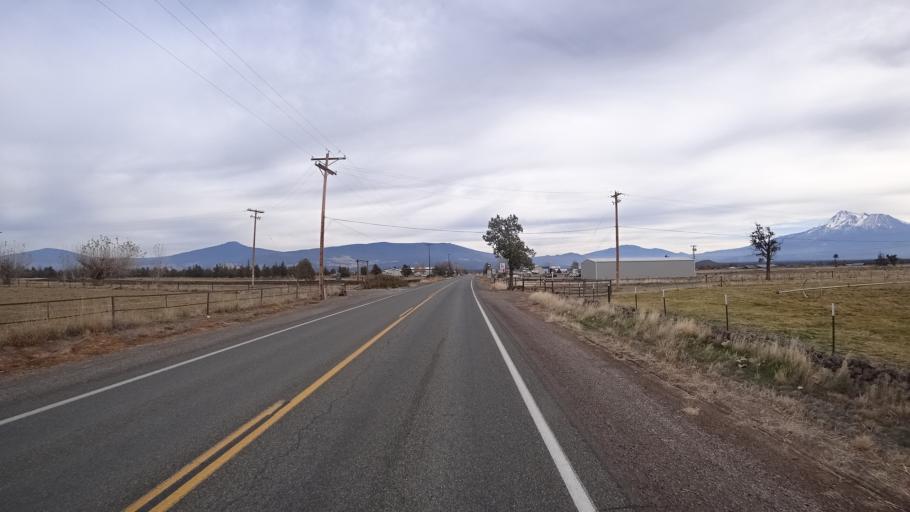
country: US
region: California
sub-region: Siskiyou County
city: Montague
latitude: 41.6241
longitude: -122.4100
